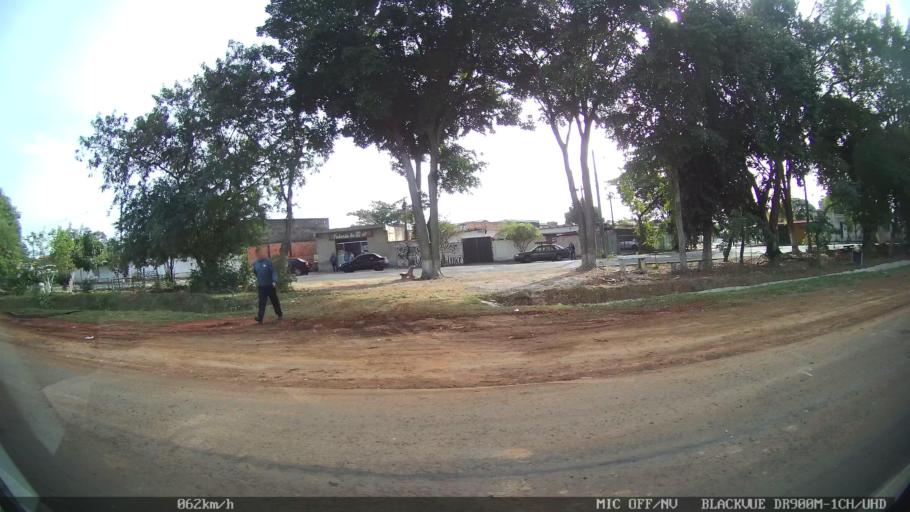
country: BR
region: Sao Paulo
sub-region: Piracicaba
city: Piracicaba
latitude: -22.6802
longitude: -47.7014
